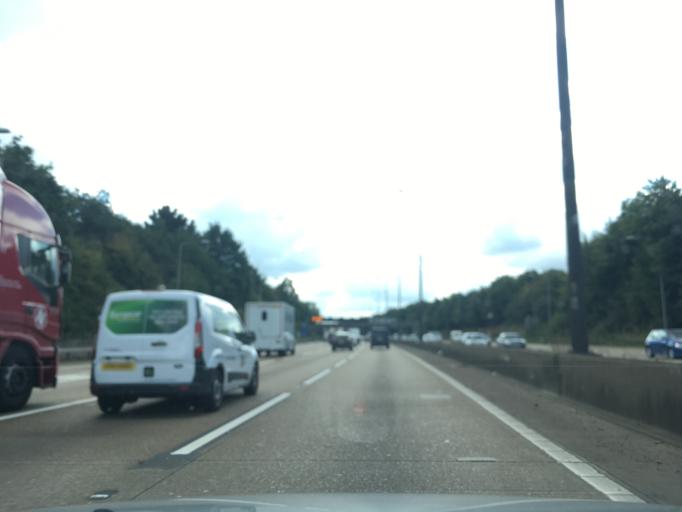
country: GB
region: England
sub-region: Surrey
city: Addlestone
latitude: 51.3702
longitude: -0.5067
